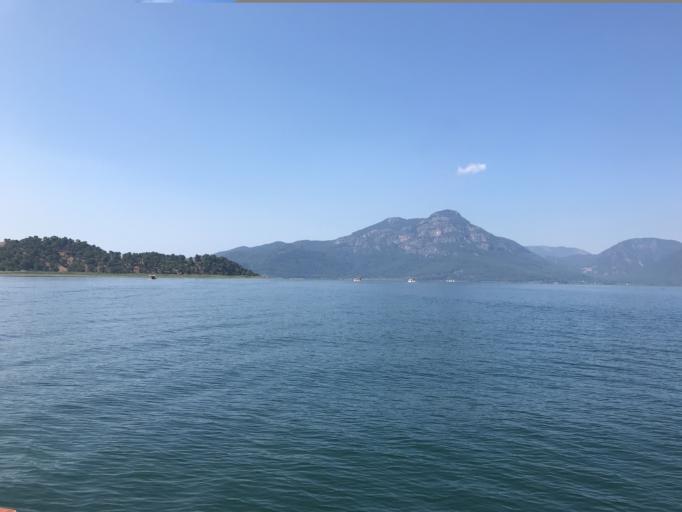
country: TR
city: Dalyan
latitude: 36.9066
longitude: 28.6499
